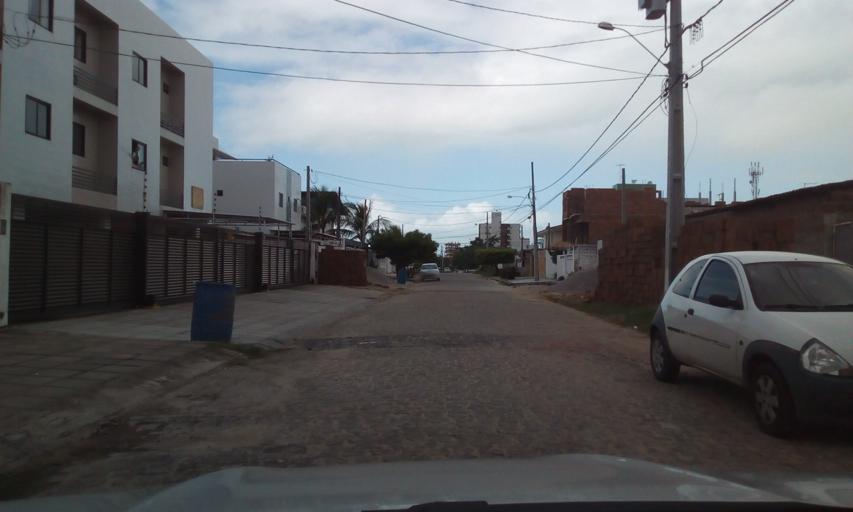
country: BR
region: Paraiba
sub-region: Joao Pessoa
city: Joao Pessoa
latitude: -7.0644
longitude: -34.8466
